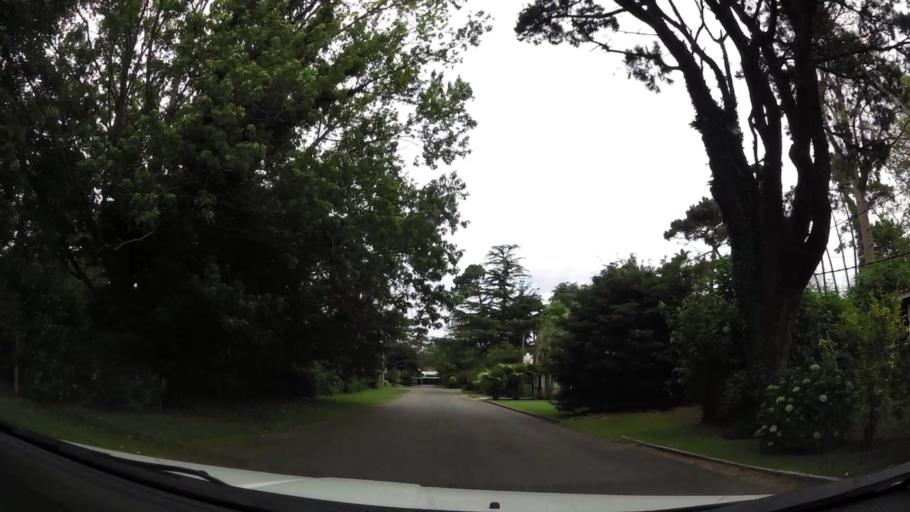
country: UY
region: Maldonado
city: Maldonado
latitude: -34.9230
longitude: -54.9544
